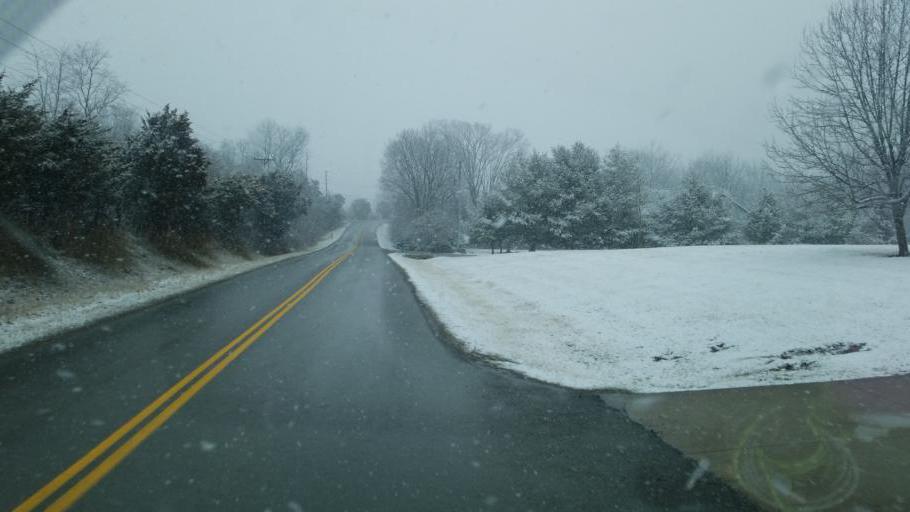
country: US
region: Ohio
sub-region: Champaign County
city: North Lewisburg
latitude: 40.3352
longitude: -83.5927
